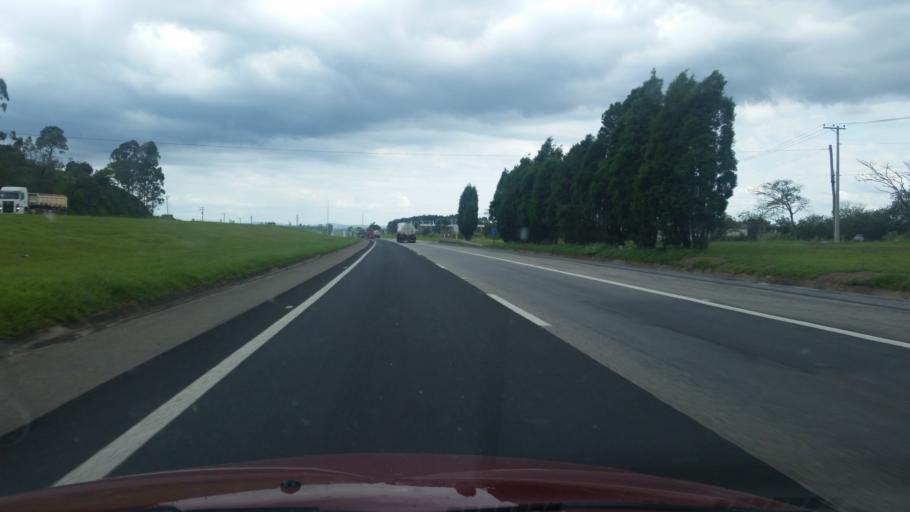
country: BR
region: Sao Paulo
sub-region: Sorocaba
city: Sorocaba
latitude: -23.3704
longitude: -47.4558
